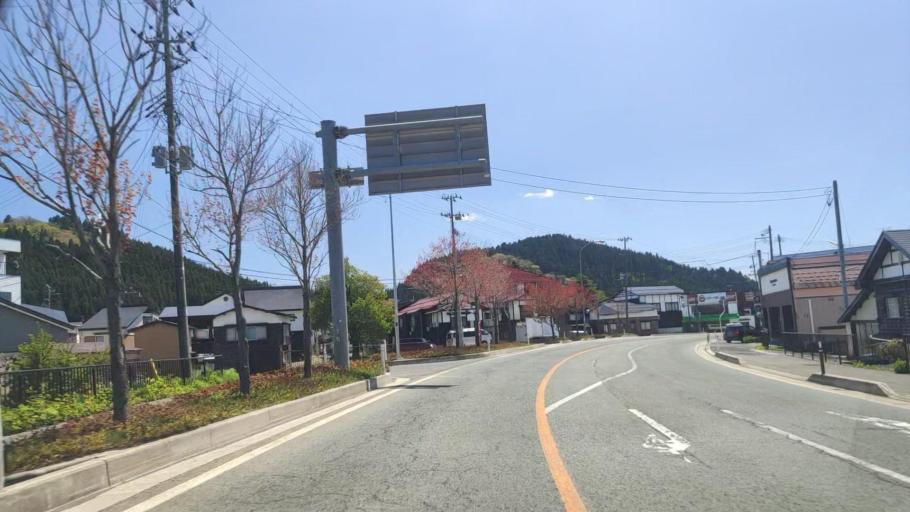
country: JP
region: Yamagata
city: Shinjo
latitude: 38.8834
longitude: 140.3366
